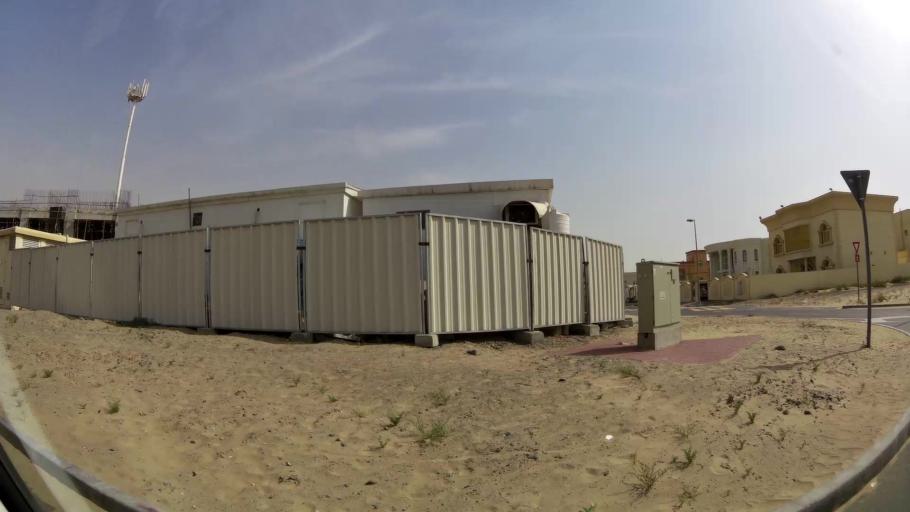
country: AE
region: Ash Shariqah
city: Sharjah
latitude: 25.2694
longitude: 55.4609
